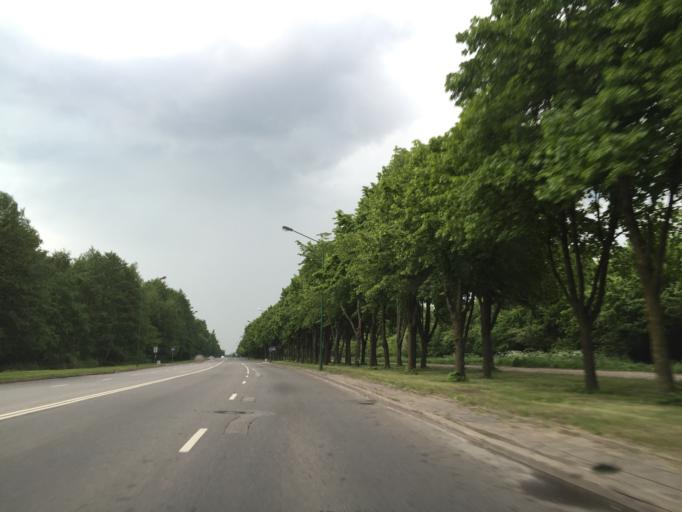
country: LT
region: Klaipedos apskritis
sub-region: Klaipeda
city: Klaipeda
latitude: 55.7359
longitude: 21.1296
